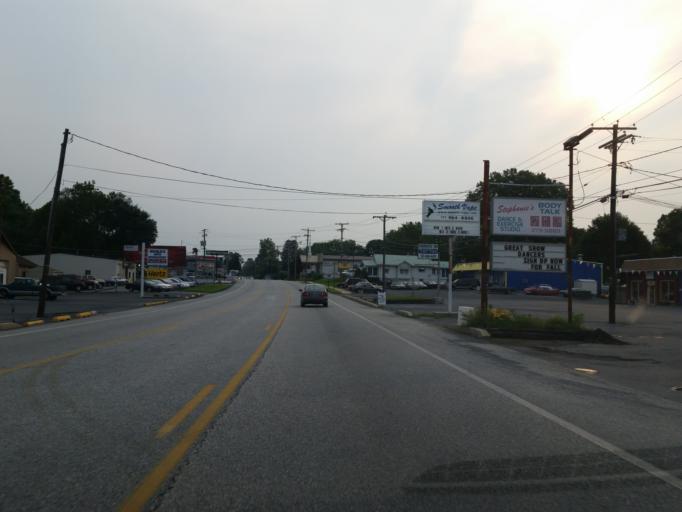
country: US
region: Pennsylvania
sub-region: Lebanon County
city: Cleona
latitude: 40.3397
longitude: -76.4601
